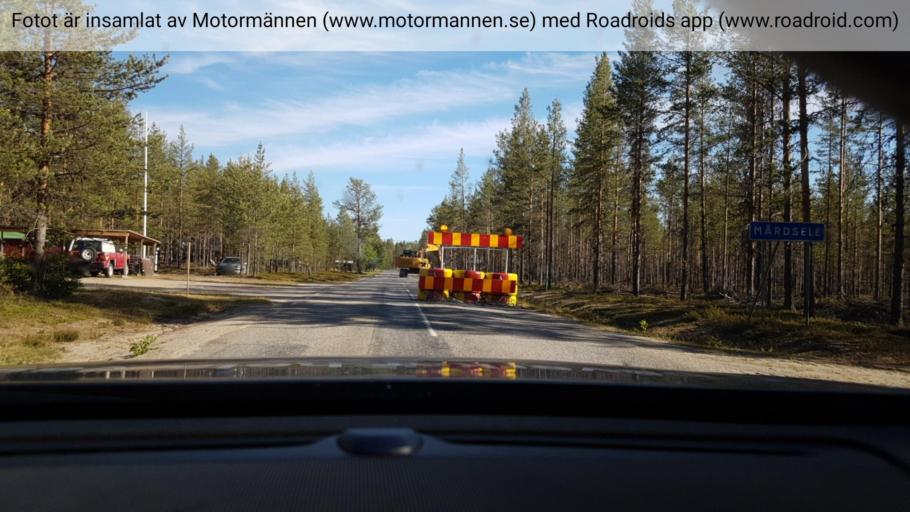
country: SE
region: Vaesterbotten
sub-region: Norsjo Kommun
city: Norsjoe
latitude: 64.6659
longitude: 19.2667
